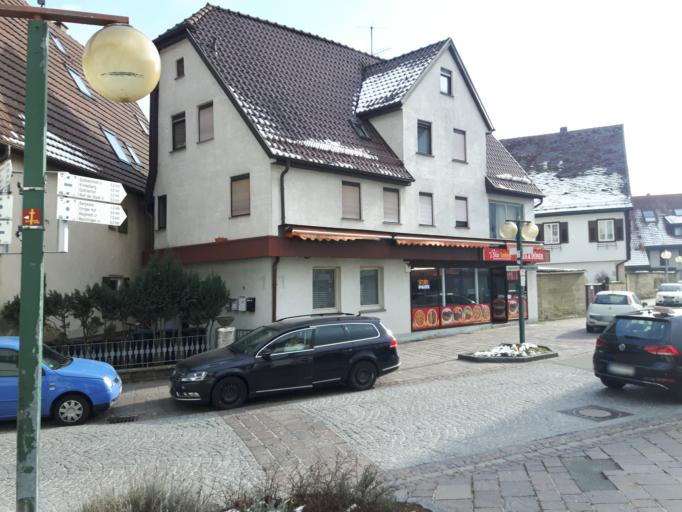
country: DE
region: Baden-Wuerttemberg
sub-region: Regierungsbezirk Stuttgart
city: Renningen
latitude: 48.7647
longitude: 8.9344
